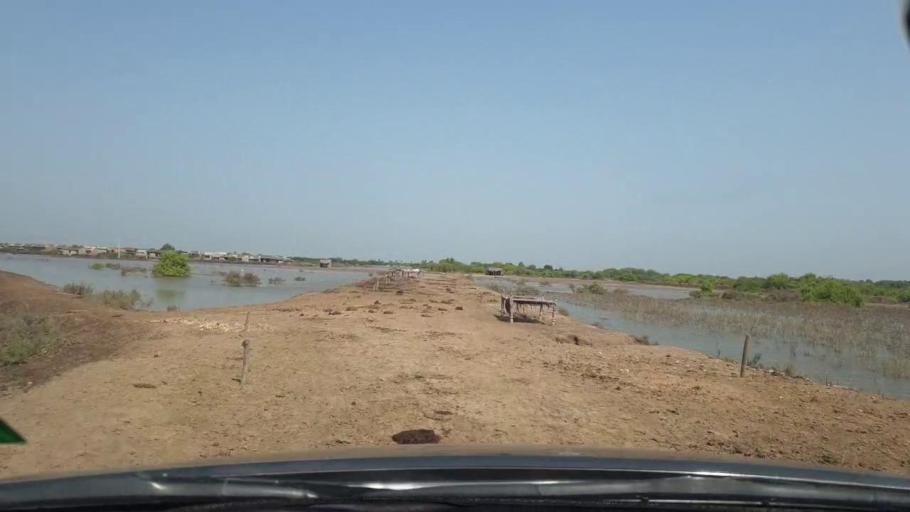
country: PK
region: Sindh
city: Tando Bago
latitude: 24.8117
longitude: 69.1120
